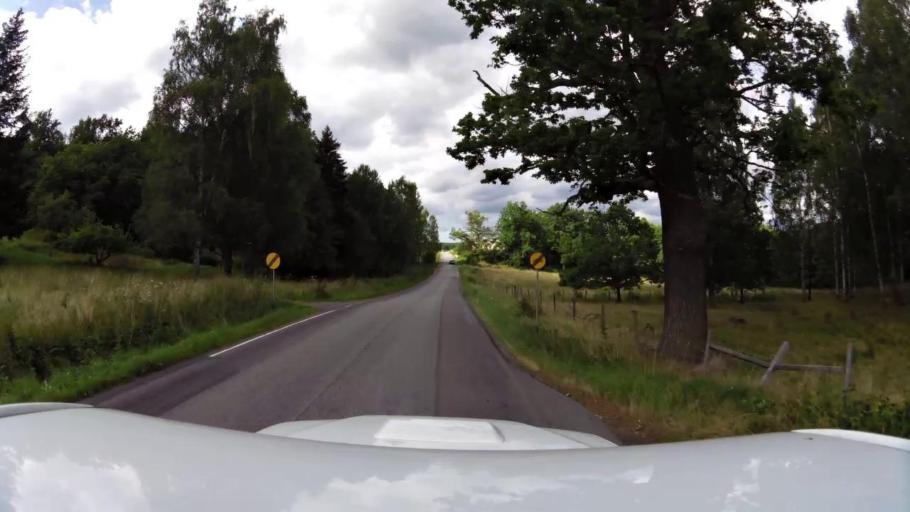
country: SE
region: OEstergoetland
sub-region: Linkopings Kommun
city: Sturefors
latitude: 58.3232
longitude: 15.7173
